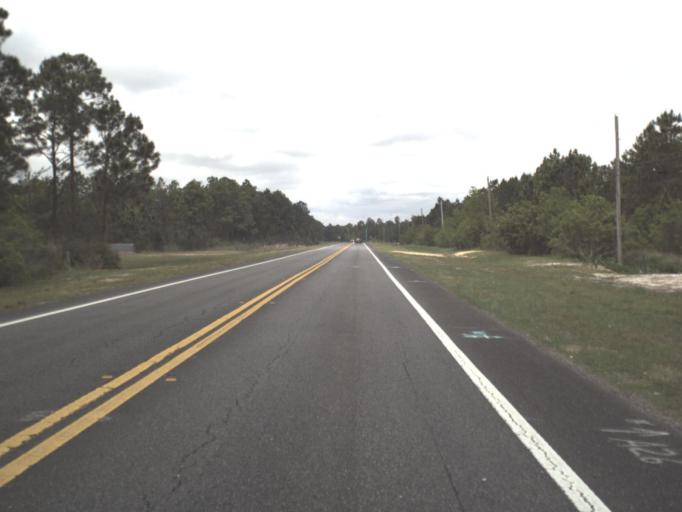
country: US
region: Florida
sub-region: Santa Rosa County
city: Bagdad
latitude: 30.5004
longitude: -87.0809
